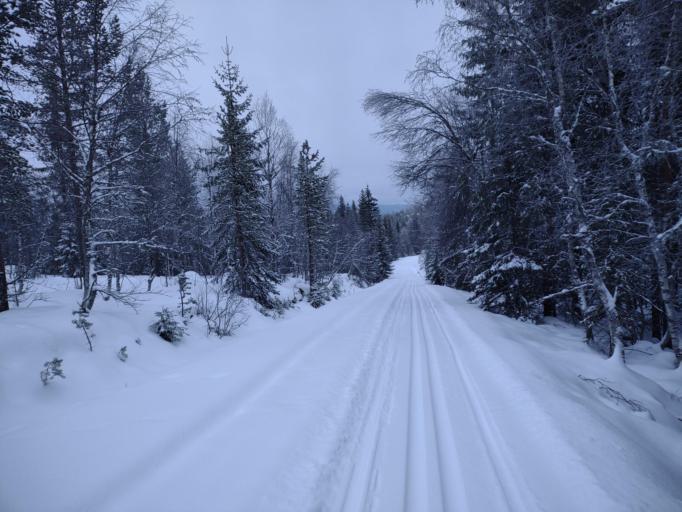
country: NO
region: Buskerud
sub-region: Flesberg
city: Lampeland
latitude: 59.7472
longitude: 9.4885
